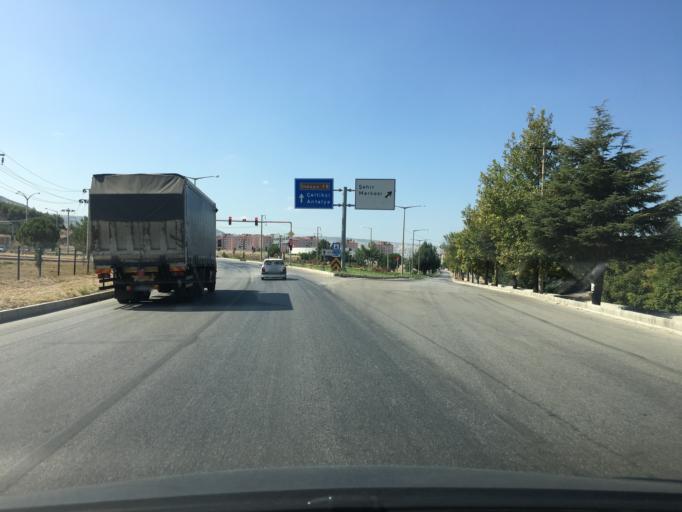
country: TR
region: Burdur
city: Burdur
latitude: 37.7418
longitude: 30.3131
